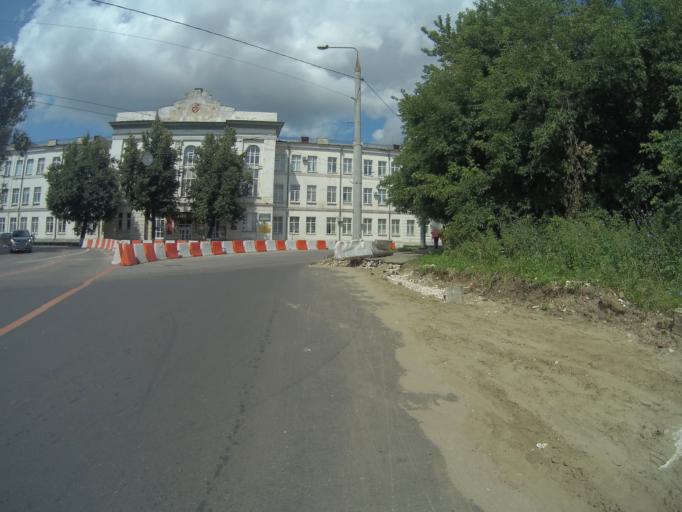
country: RU
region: Vladimir
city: Vladimir
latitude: 56.1349
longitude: 40.4070
